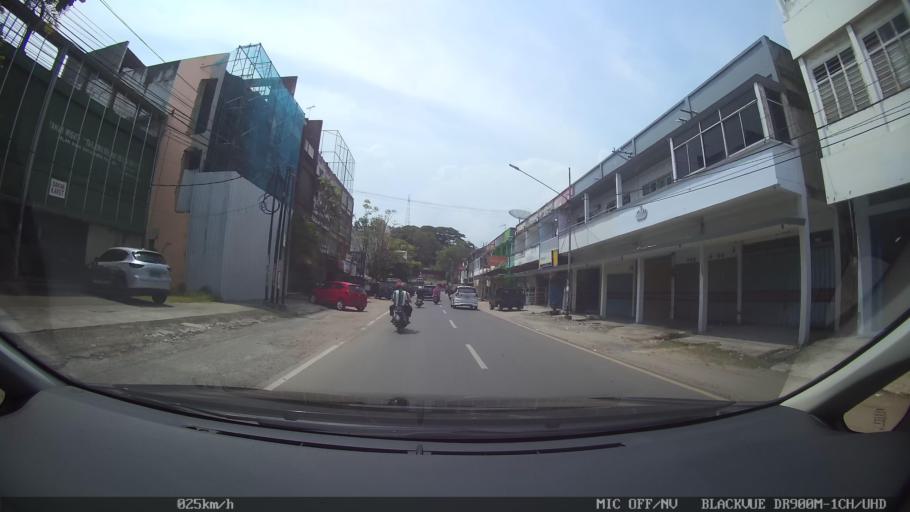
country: ID
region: Lampung
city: Bandarlampung
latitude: -5.4479
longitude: 105.2620
